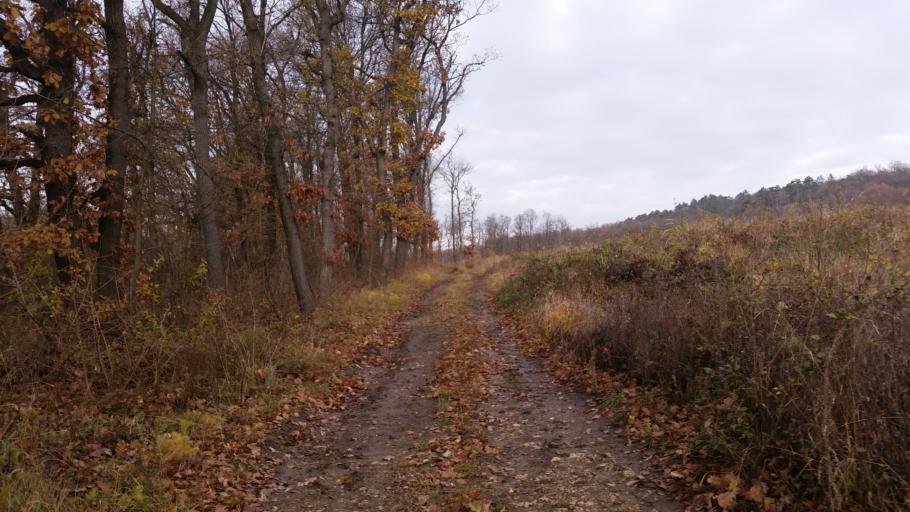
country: HU
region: Pest
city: Telki
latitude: 47.5663
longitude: 18.8204
